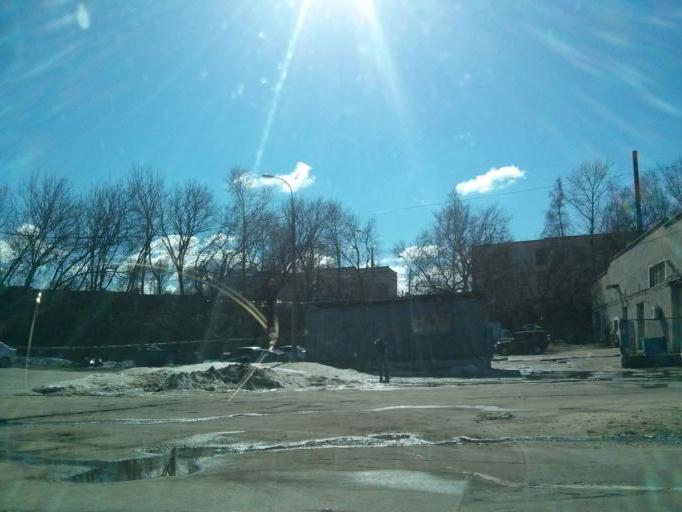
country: RU
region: Nizjnij Novgorod
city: Bor
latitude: 56.3101
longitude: 44.0691
